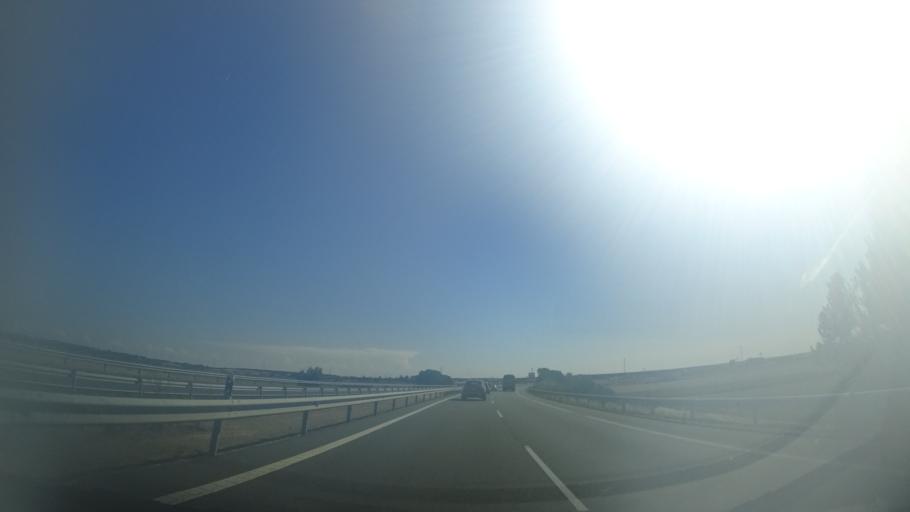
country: ES
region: Castille and Leon
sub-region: Provincia de Valladolid
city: Tordesillas
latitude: 41.4881
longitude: -4.9849
